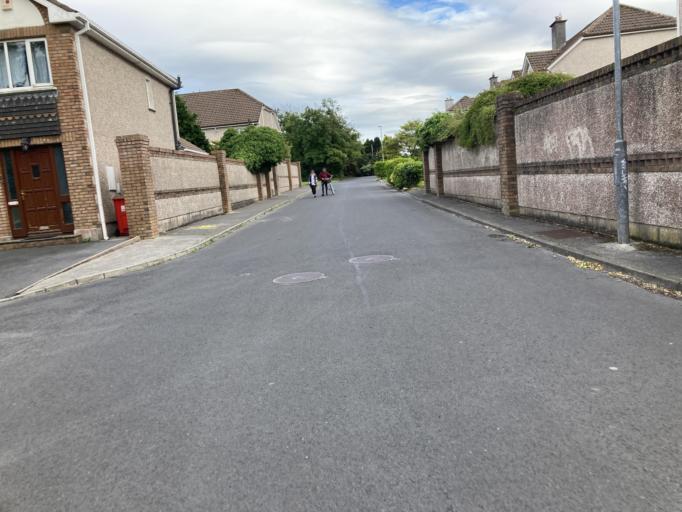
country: IE
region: Connaught
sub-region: County Galway
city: Bearna
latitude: 53.2633
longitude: -9.1212
